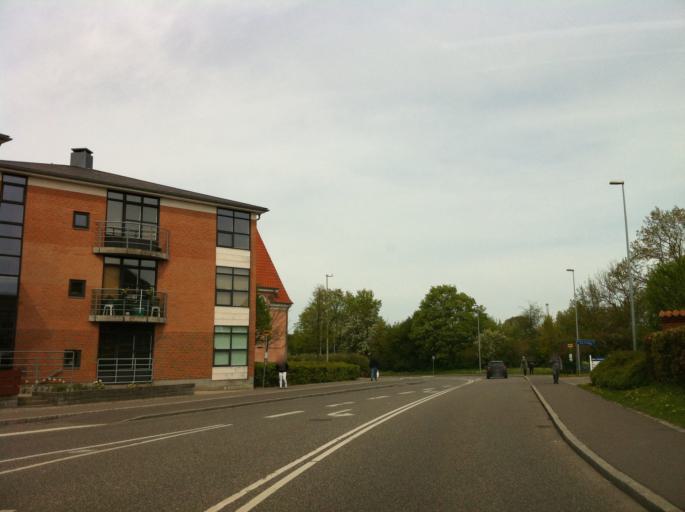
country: DK
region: Zealand
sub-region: Naestved Kommune
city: Naestved
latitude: 55.2339
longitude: 11.7611
